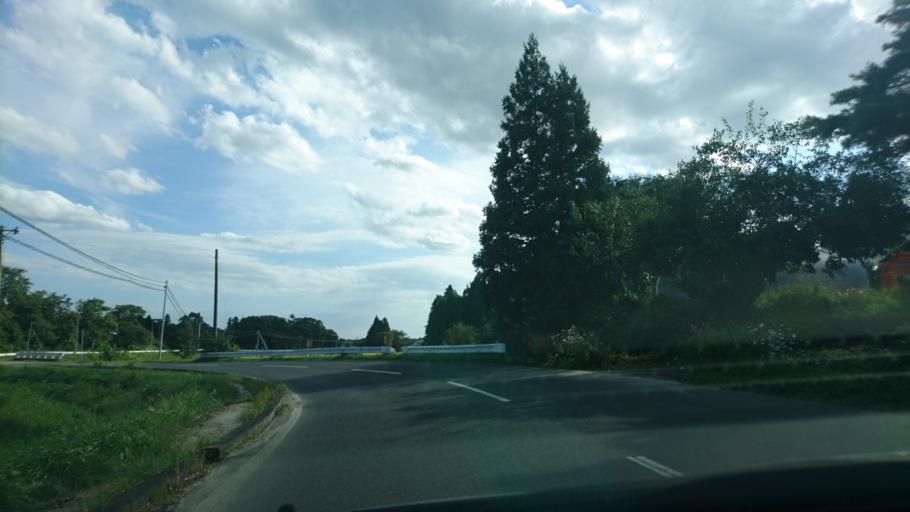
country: JP
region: Iwate
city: Ichinoseki
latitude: 38.8390
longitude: 141.1916
